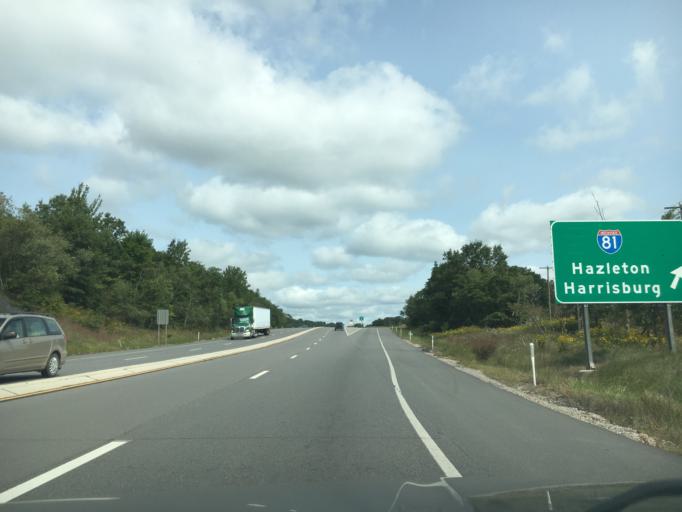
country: US
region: Pennsylvania
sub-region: Schuylkill County
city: McAdoo
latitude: 40.8775
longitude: -76.0034
